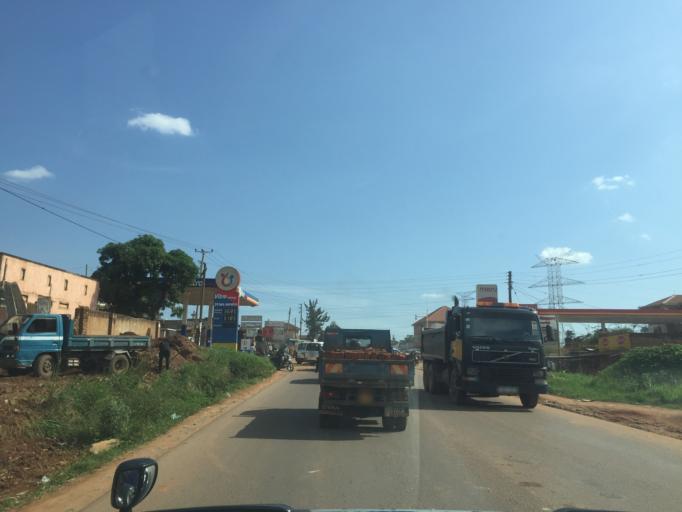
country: UG
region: Central Region
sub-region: Wakiso District
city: Wakiso
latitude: 0.4170
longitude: 32.5370
